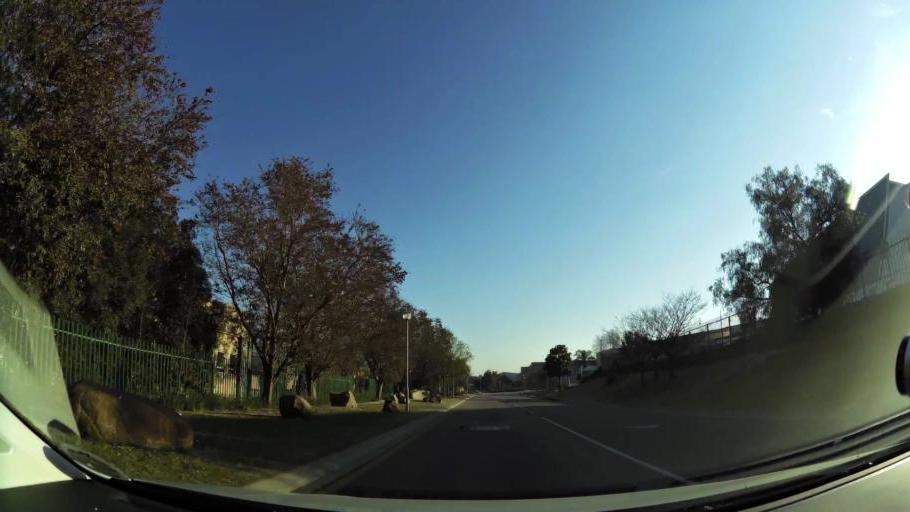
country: ZA
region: Gauteng
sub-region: City of Johannesburg Metropolitan Municipality
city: Modderfontein
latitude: -26.0687
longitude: 28.1125
